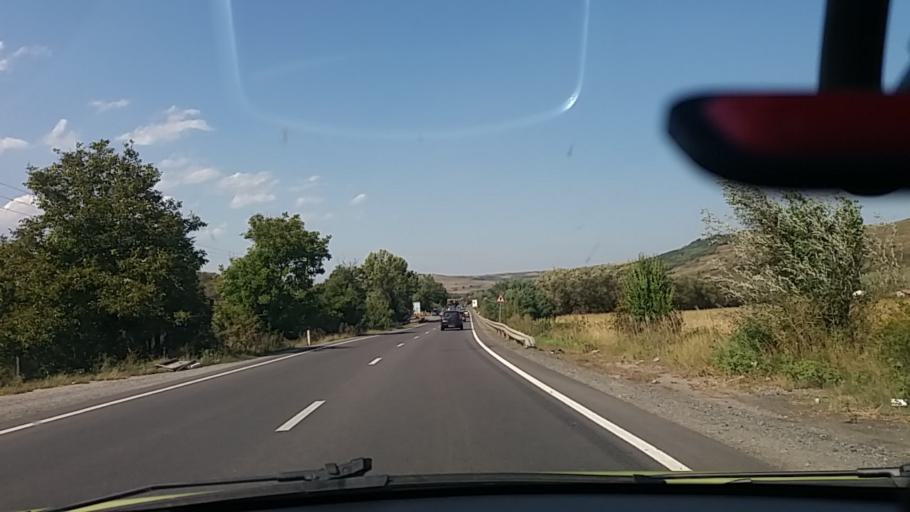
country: RO
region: Sibiu
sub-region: Comuna Slimnic
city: Slimnic
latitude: 45.8966
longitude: 24.1617
